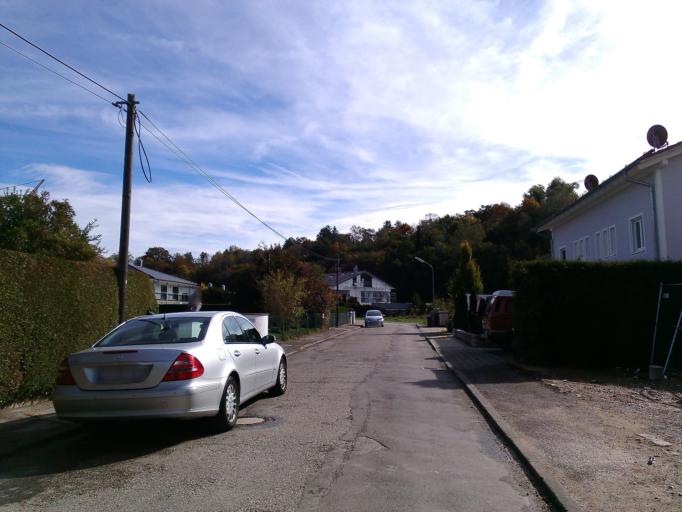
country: DE
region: Bavaria
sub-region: Upper Bavaria
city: Gauting
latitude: 48.0645
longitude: 11.3842
